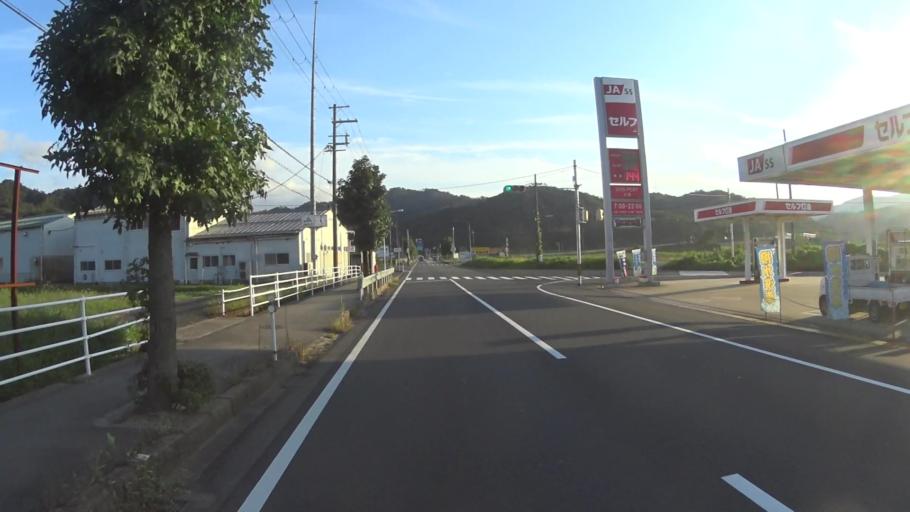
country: JP
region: Kyoto
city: Miyazu
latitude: 35.5707
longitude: 135.0972
